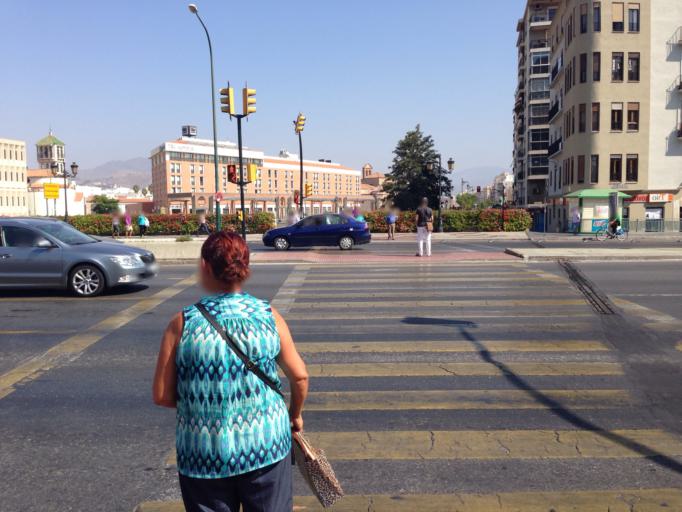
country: ES
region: Andalusia
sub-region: Provincia de Malaga
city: Malaga
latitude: 36.7167
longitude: -4.4256
